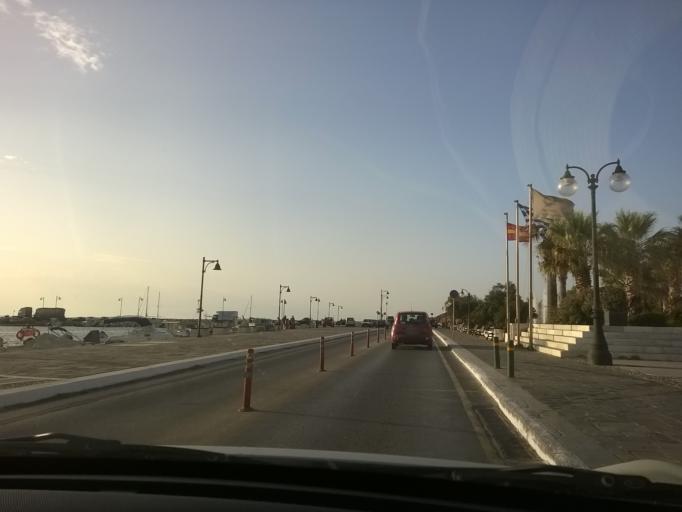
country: GR
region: South Aegean
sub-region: Nomos Kykladon
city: Naxos
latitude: 37.1066
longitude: 25.3746
